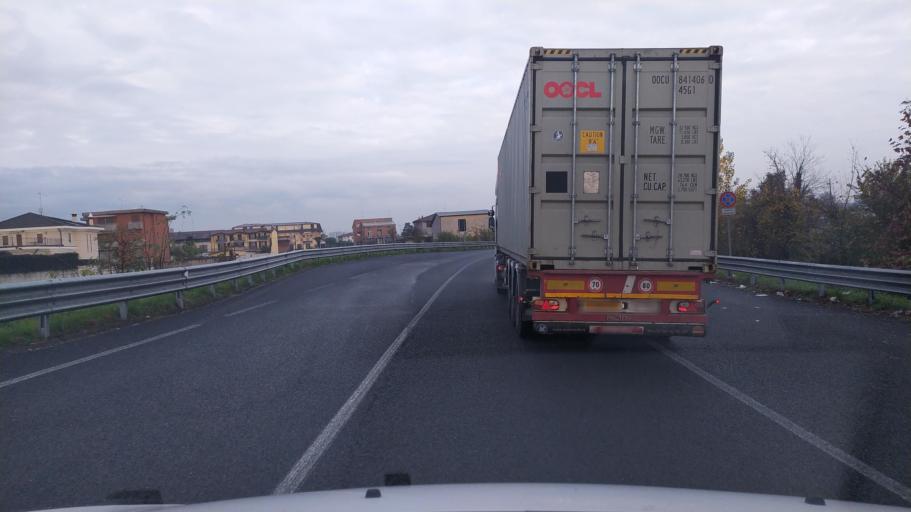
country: IT
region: Lombardy
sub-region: Provincia di Bergamo
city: Calcio
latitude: 45.5068
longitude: 9.8584
